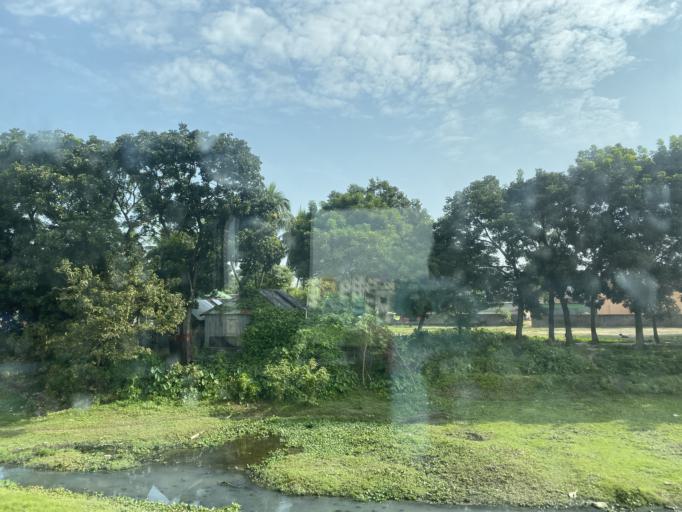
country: BD
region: Chittagong
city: Nabinagar
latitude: 23.9624
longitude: 91.1181
